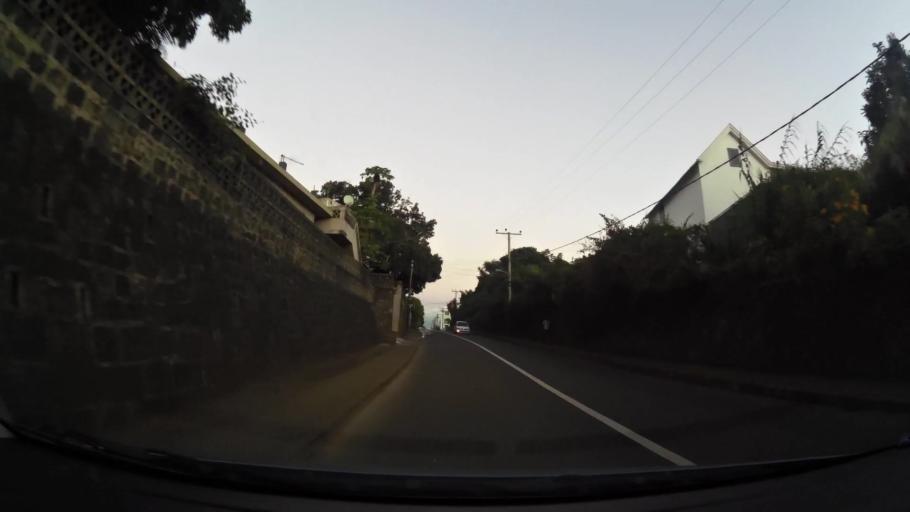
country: MU
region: Moka
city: Moka
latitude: -20.2200
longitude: 57.5013
